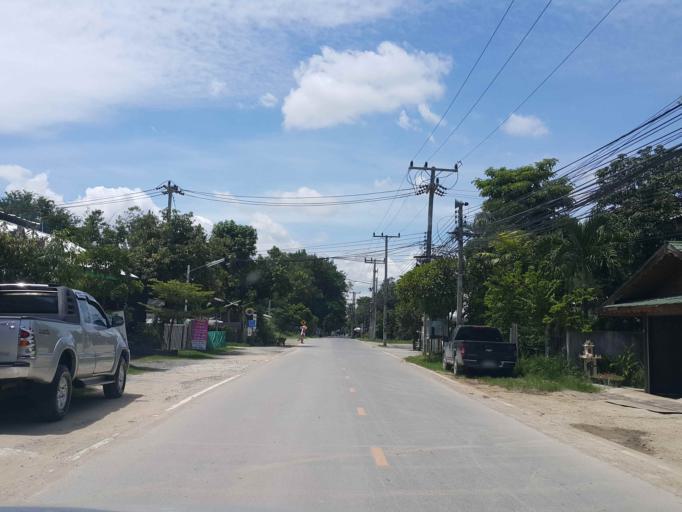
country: TH
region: Chiang Mai
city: San Sai
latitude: 18.8002
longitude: 99.0606
